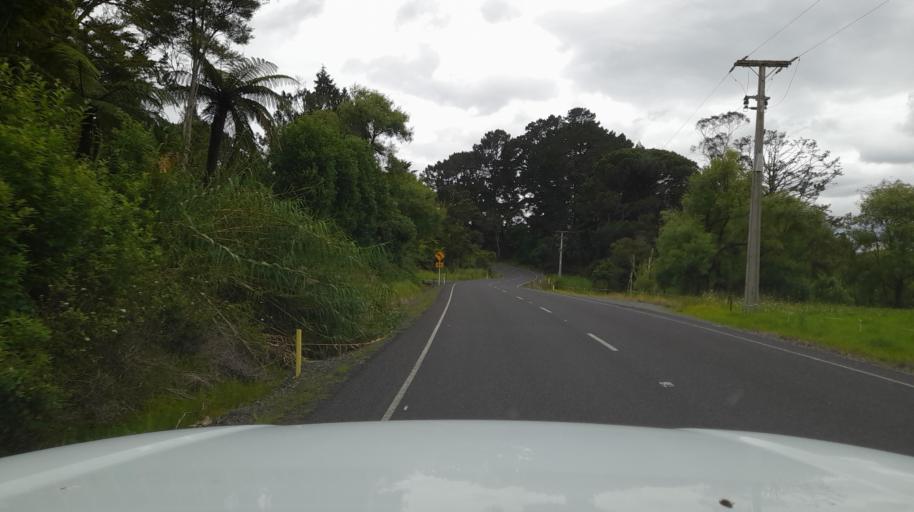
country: NZ
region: Northland
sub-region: Far North District
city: Taipa
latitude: -35.2411
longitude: 173.5398
